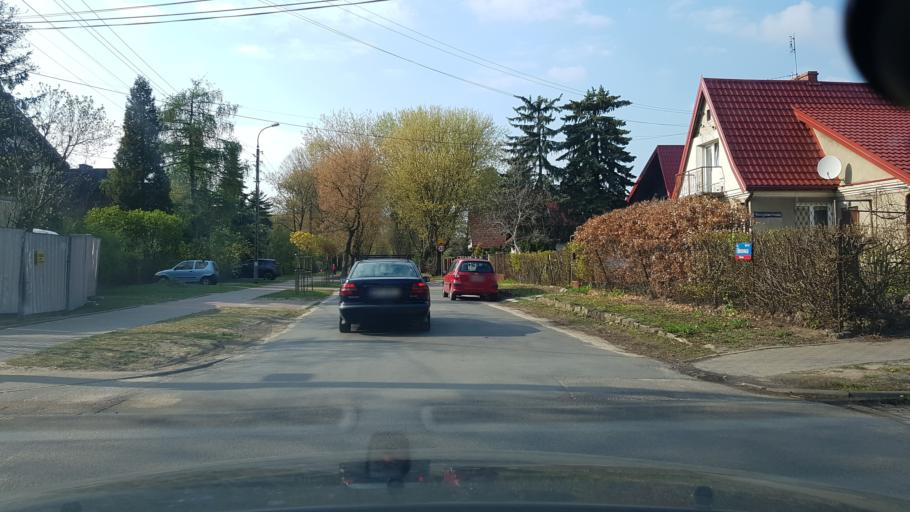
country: PL
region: Masovian Voivodeship
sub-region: Powiat otwocki
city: Jozefow
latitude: 52.1637
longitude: 21.2152
